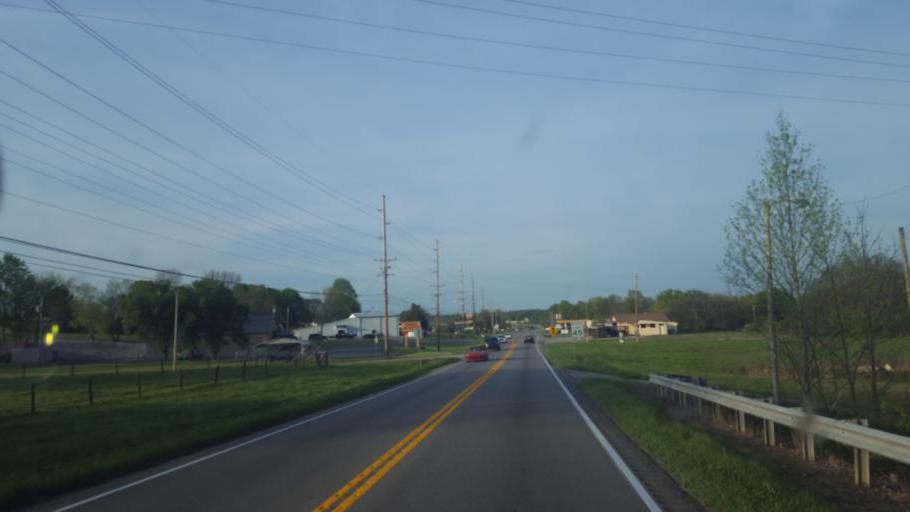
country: US
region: Kentucky
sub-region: Barren County
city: Glasgow
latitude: 36.9695
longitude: -85.9428
